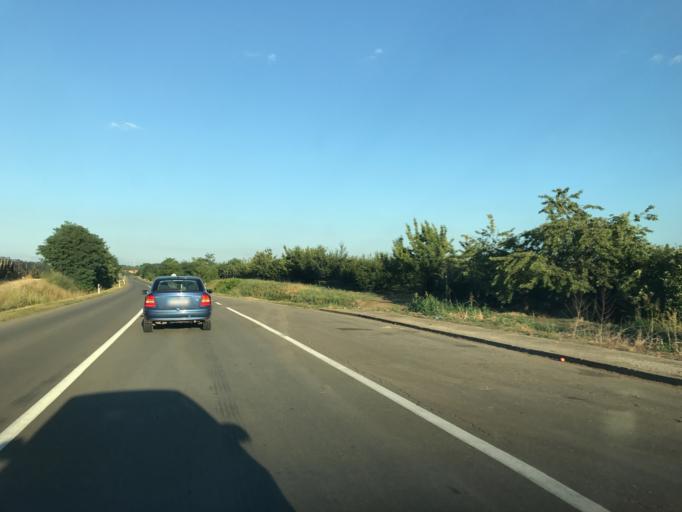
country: RS
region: Central Serbia
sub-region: Podunavski Okrug
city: Smederevo
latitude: 44.6310
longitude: 20.8566
